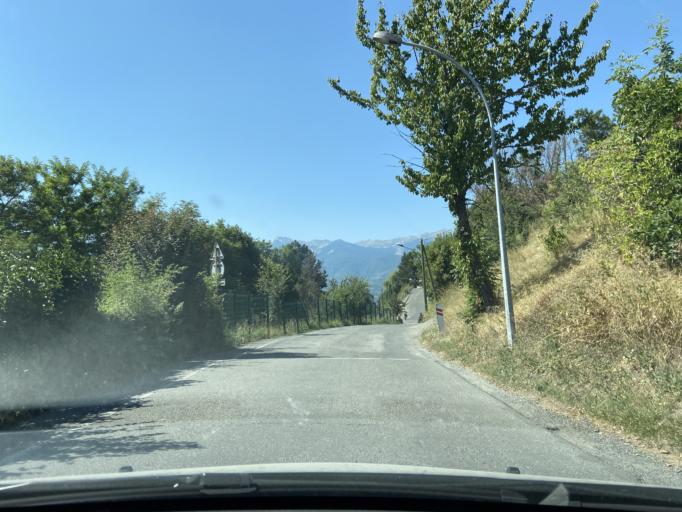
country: FR
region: Provence-Alpes-Cote d'Azur
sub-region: Departement des Hautes-Alpes
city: Embrun
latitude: 44.5642
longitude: 6.4917
